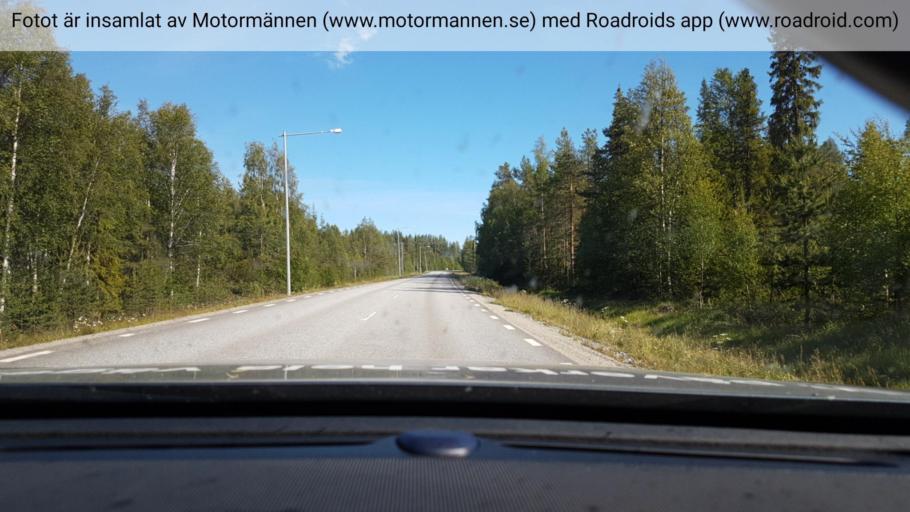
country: SE
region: Vaesterbotten
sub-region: Lycksele Kommun
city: Lycksele
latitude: 64.6931
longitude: 18.3975
